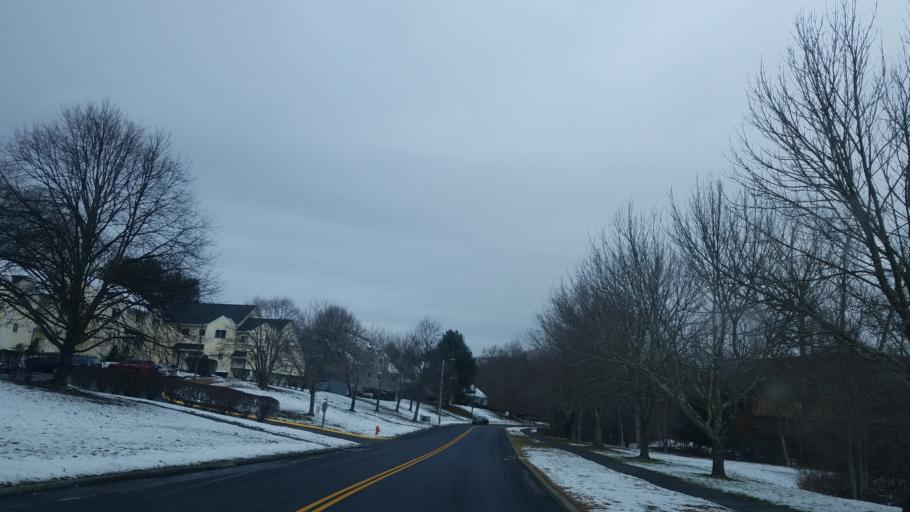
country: US
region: Connecticut
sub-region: New London County
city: Central Waterford
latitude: 41.3502
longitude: -72.1595
